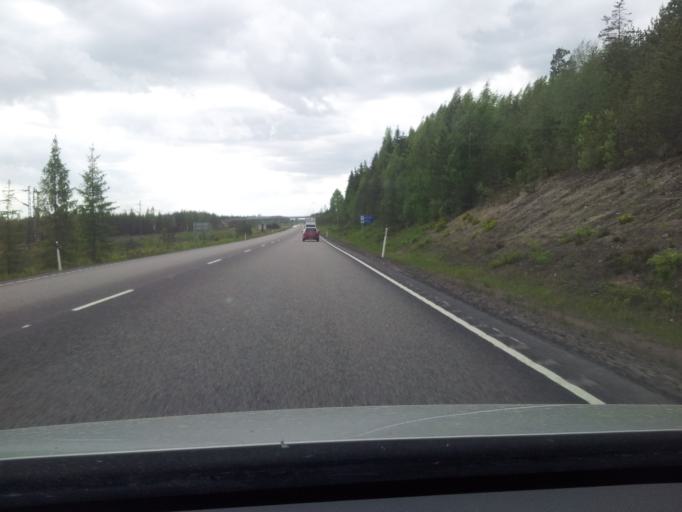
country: FI
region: Kymenlaakso
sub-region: Kotka-Hamina
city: Hamina
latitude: 60.9048
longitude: 27.2146
